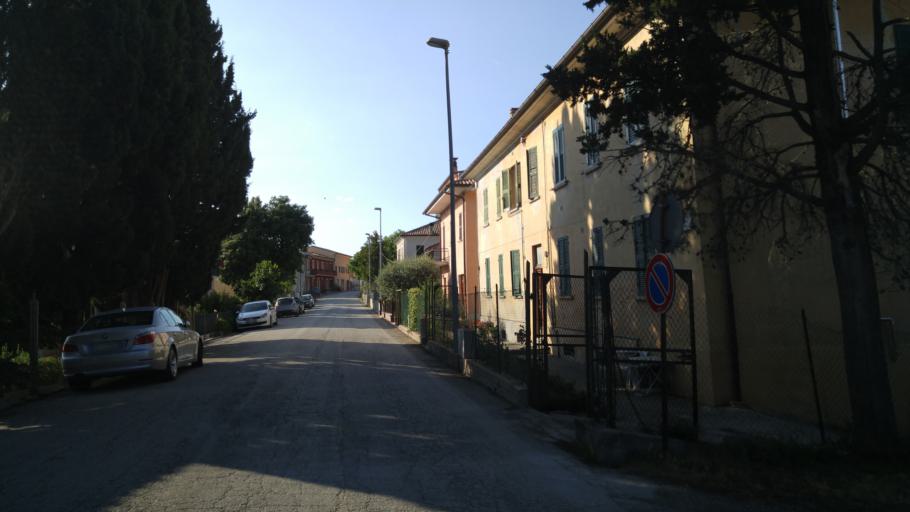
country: IT
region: The Marches
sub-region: Provincia di Pesaro e Urbino
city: Sant'Ippolito
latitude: 43.6829
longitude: 12.8717
